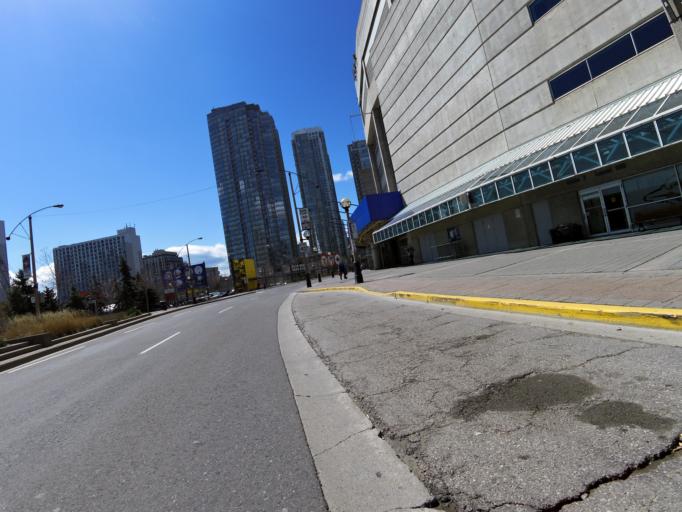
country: CA
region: Ontario
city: Toronto
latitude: 43.6407
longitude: -79.3881
